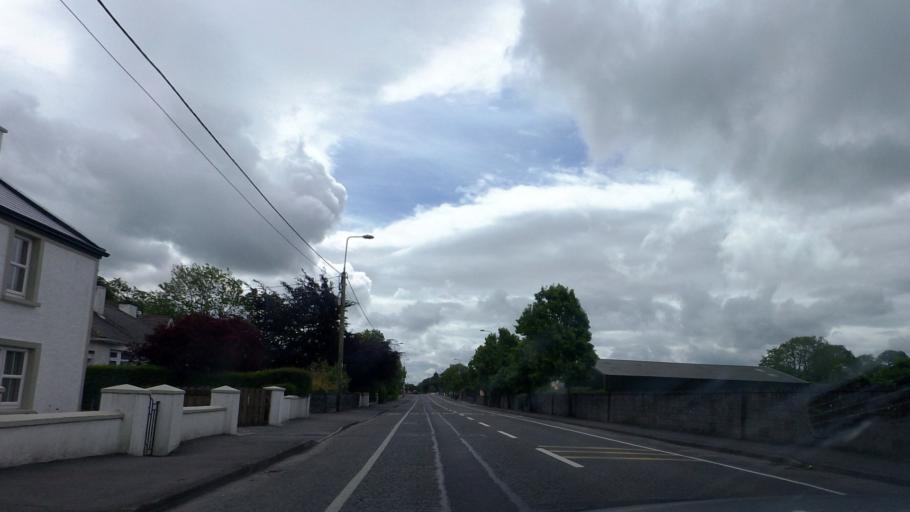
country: IE
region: Munster
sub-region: An Clar
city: Ennis
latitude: 52.8283
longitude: -8.9789
